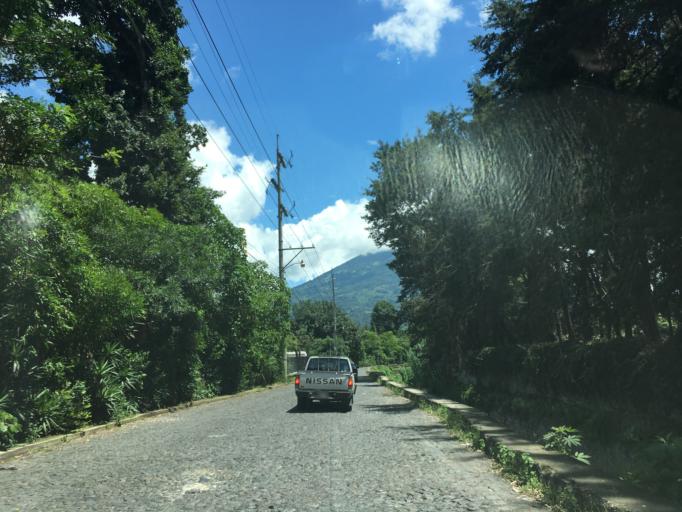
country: GT
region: Sacatepequez
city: Antigua Guatemala
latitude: 14.5524
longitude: -90.7273
